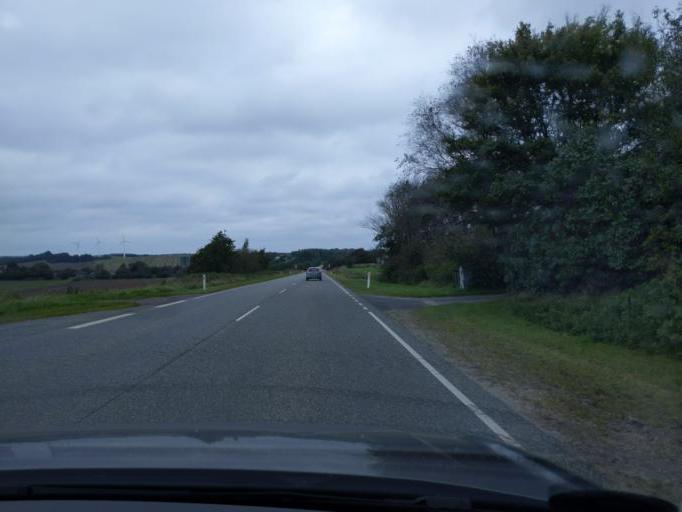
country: DK
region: North Denmark
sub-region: Mariagerfjord Kommune
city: Hobro
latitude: 56.5659
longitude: 9.8313
